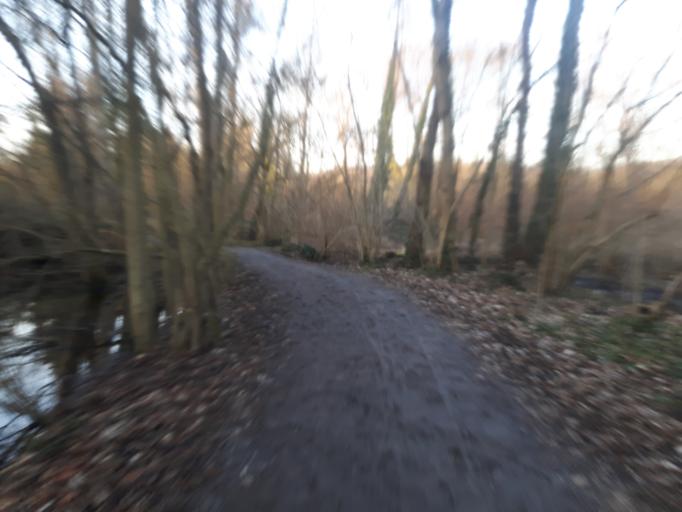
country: DE
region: Baden-Wuerttemberg
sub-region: Regierungsbezirk Stuttgart
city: Heilbronn
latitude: 49.1350
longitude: 9.2544
